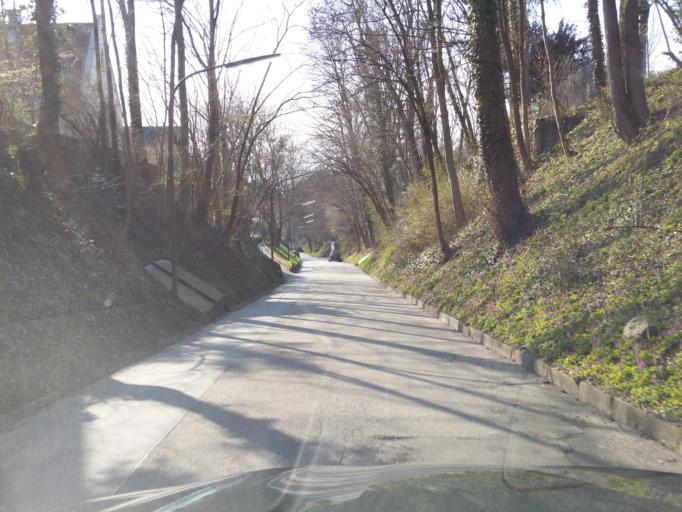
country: DE
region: Bavaria
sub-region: Lower Bavaria
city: Landshut
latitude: 48.5284
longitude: 12.1592
